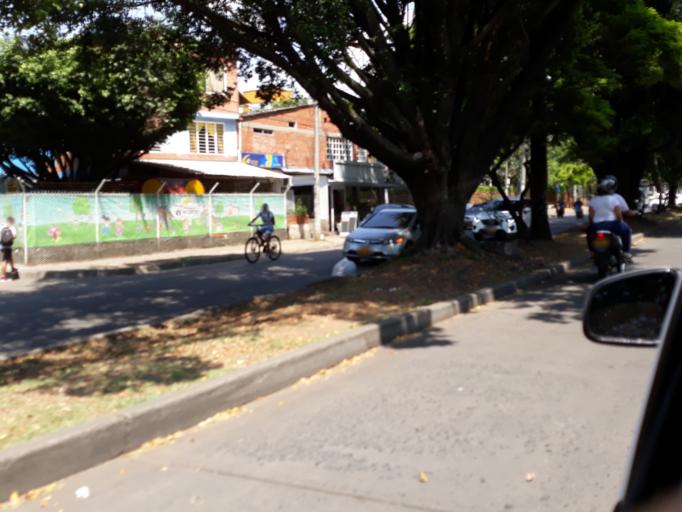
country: CO
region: Valle del Cauca
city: Cali
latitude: 3.4796
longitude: -76.4967
